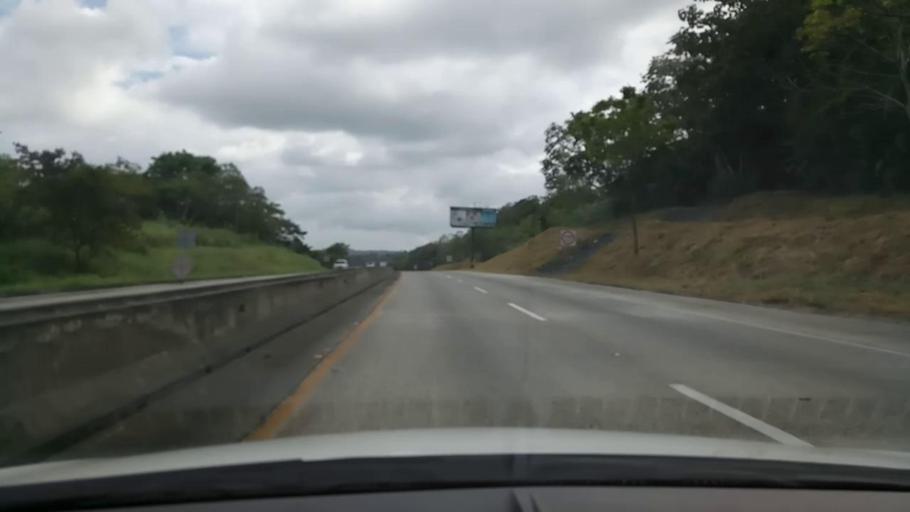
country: PA
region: Panama
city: Chilibre
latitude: 9.1635
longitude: -79.6391
